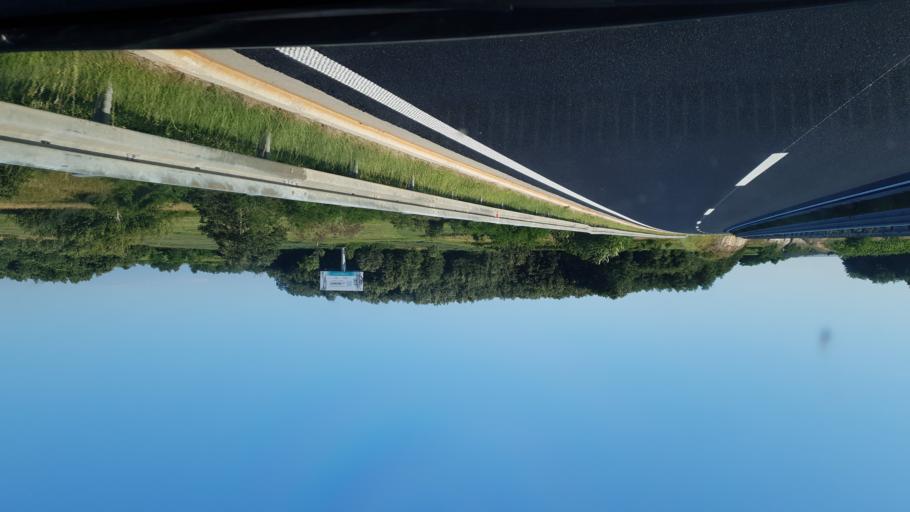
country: HR
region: Istarska
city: Pazin
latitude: 45.1971
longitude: 13.8935
